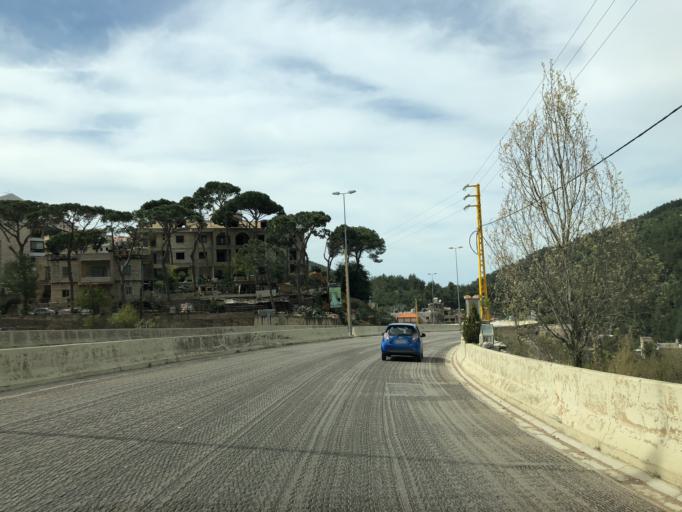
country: LB
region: Mont-Liban
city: Bhamdoun el Mhatta
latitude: 33.8913
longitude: 35.6603
